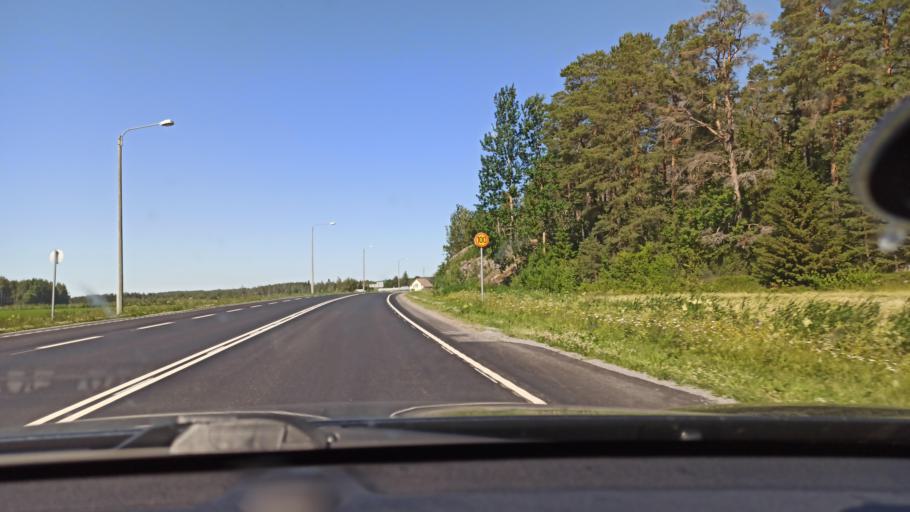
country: FI
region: Ostrobothnia
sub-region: Vaasa
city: Oravais
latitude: 63.3156
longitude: 22.3911
